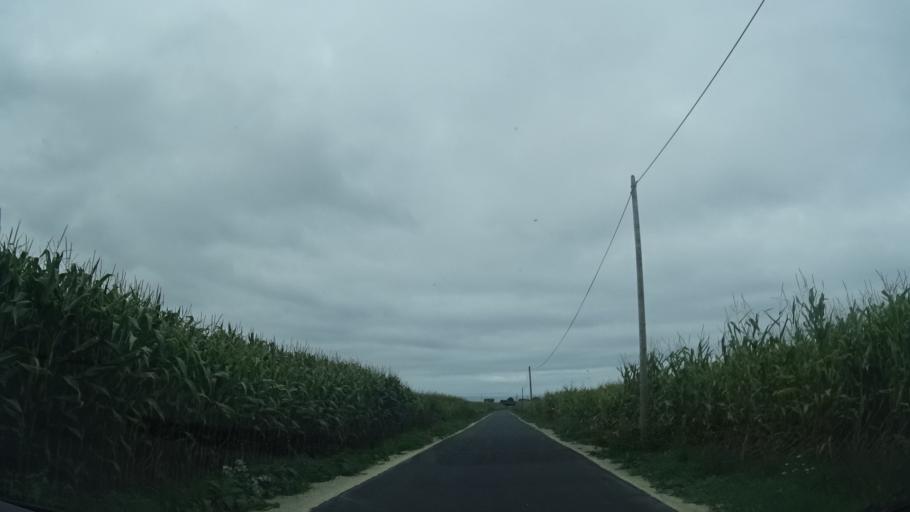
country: FR
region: Brittany
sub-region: Departement du Finistere
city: Lampaul-Plouarzel
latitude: 48.4578
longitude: -4.7402
